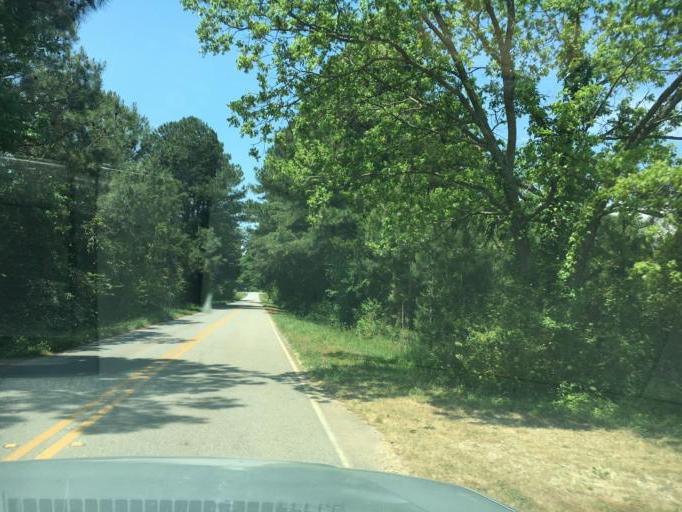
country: US
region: Georgia
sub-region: Hart County
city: Royston
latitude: 34.3054
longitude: -83.0967
